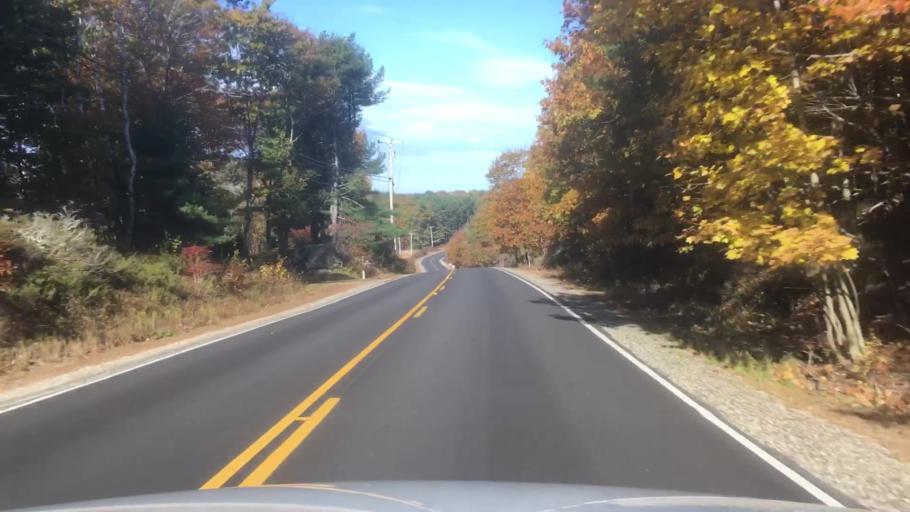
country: US
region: Maine
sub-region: Sagadahoc County
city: Phippsburg
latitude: 43.8555
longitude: -69.7802
